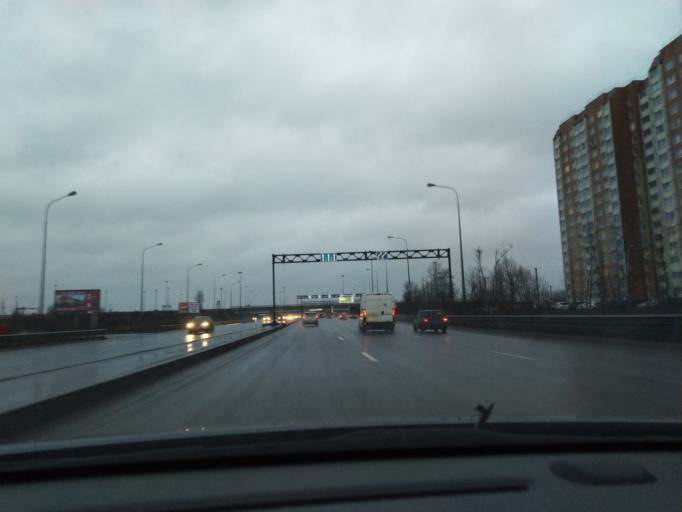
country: RU
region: St.-Petersburg
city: Gorelovo
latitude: 59.7951
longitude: 30.1510
